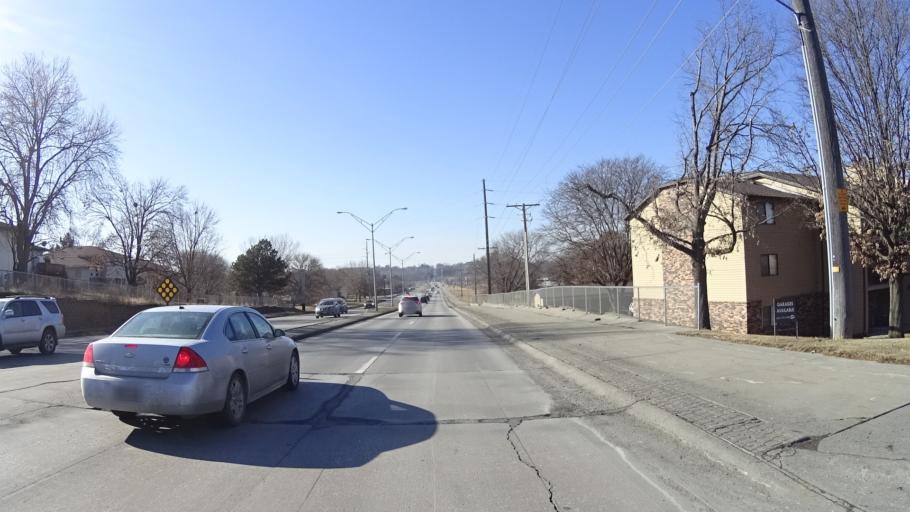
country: US
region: Nebraska
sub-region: Douglas County
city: Bennington
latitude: 41.3067
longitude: -96.0925
